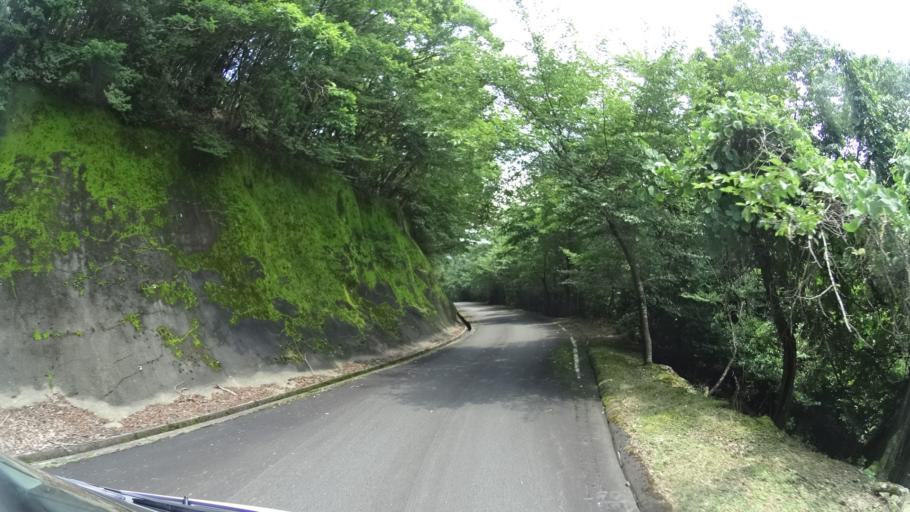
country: JP
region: Hyogo
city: Sasayama
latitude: 35.1684
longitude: 135.2024
